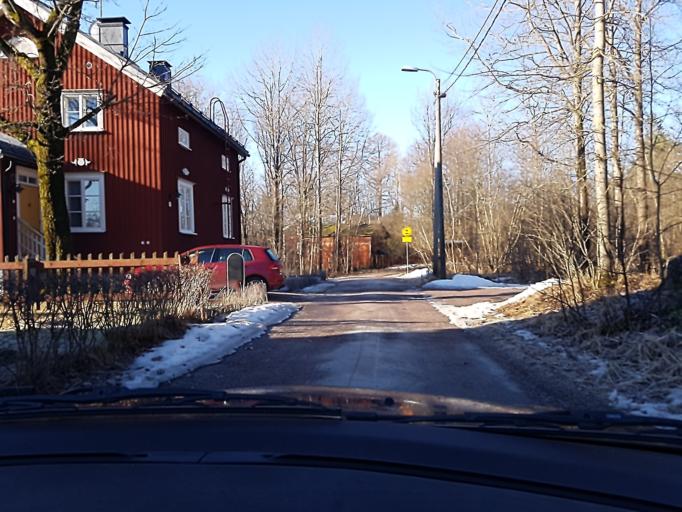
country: FI
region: Uusimaa
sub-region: Helsinki
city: Helsinki
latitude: 60.2068
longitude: 24.9572
